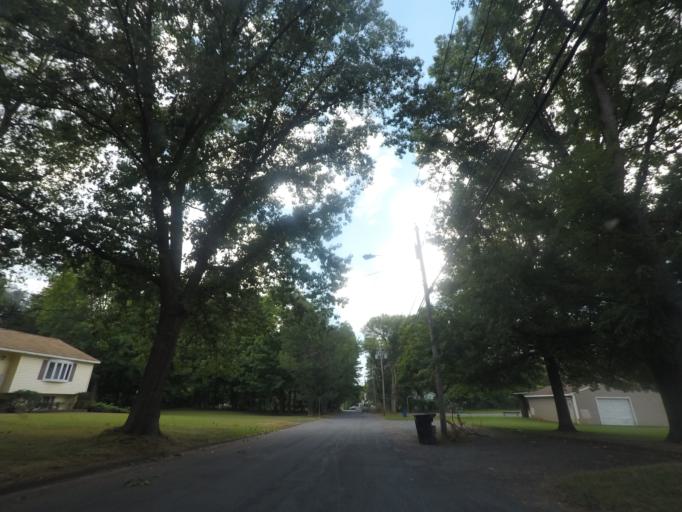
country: US
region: New York
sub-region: Rensselaer County
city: Troy
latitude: 42.7062
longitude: -73.6905
